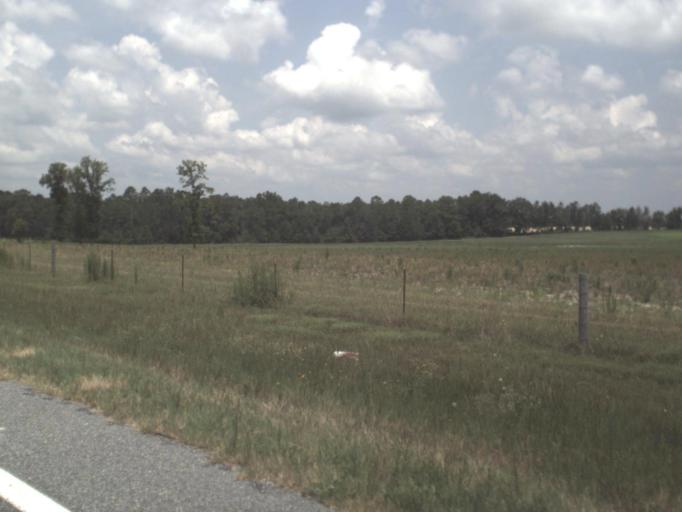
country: US
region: Florida
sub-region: Hamilton County
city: Jasper
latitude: 30.4901
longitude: -83.1406
